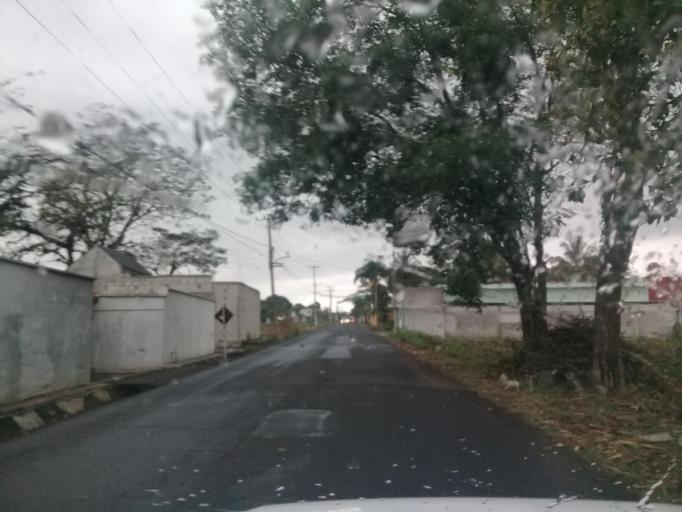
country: MX
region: Veracruz
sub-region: Cordoba
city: Veinte de Noviembre
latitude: 18.8602
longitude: -96.9521
